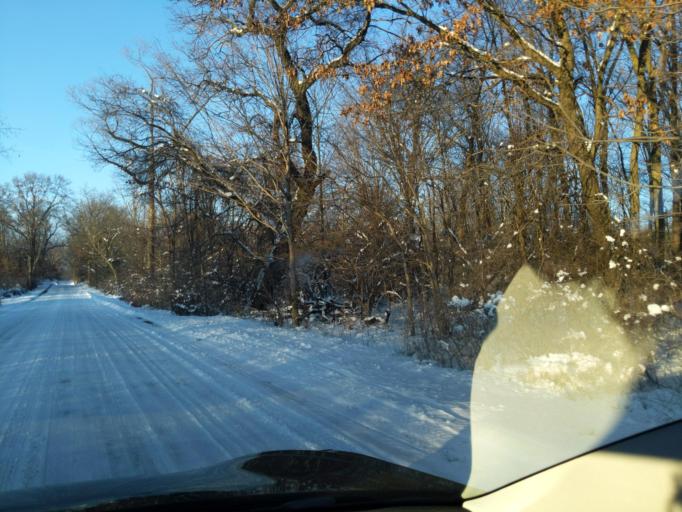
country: US
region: Michigan
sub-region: Ingham County
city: Stockbridge
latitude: 42.5255
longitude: -84.1171
